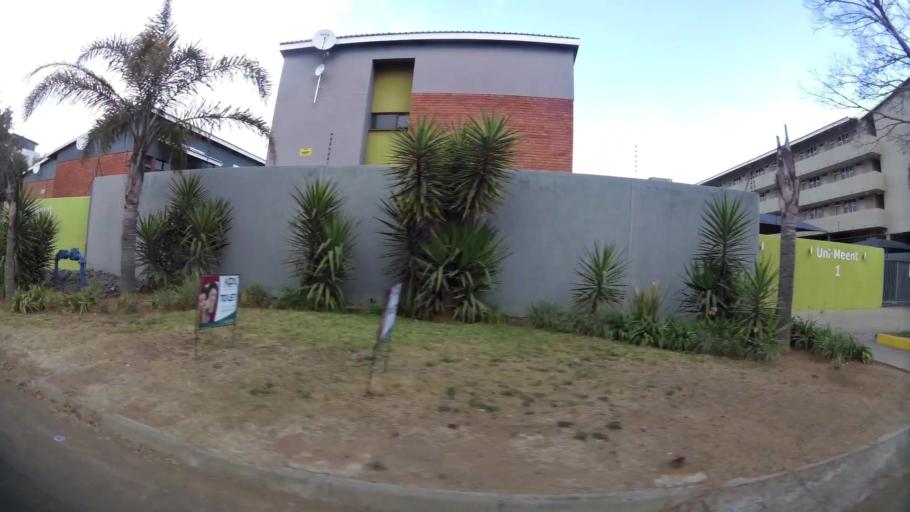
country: ZA
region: Orange Free State
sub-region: Mangaung Metropolitan Municipality
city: Bloemfontein
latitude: -29.1167
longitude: 26.1885
